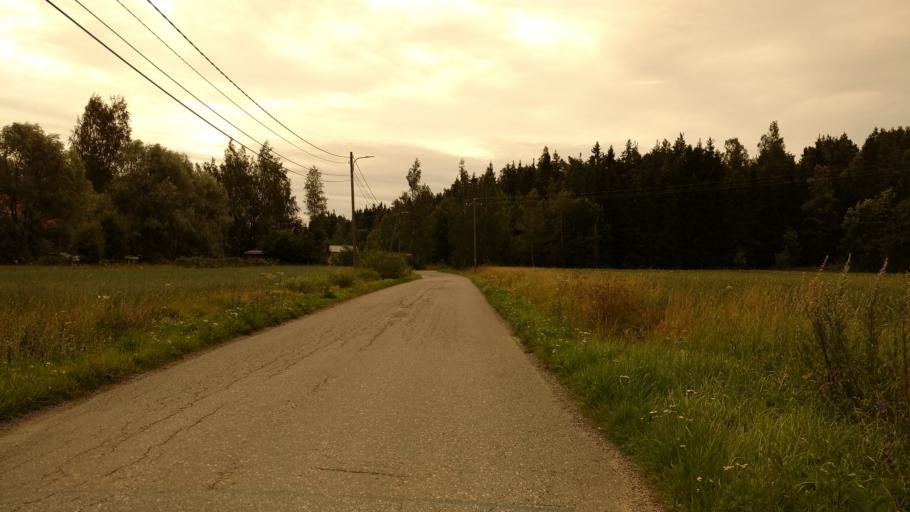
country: FI
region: Varsinais-Suomi
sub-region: Turku
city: Kaarina
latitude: 60.4420
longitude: 22.4334
